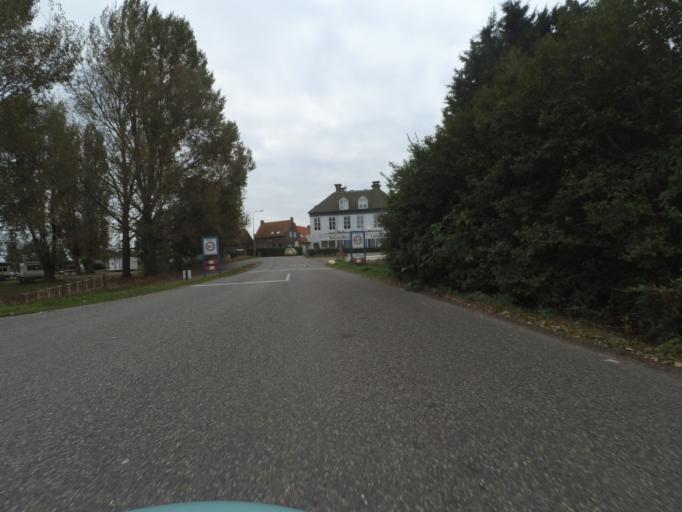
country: NL
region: Gelderland
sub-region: Gemeente Culemborg
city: Culemborg
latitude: 51.9623
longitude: 5.2810
